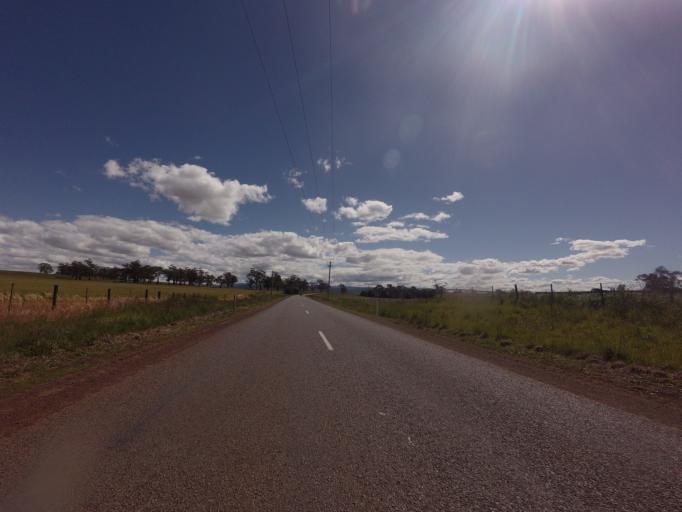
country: AU
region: Tasmania
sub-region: Northern Midlands
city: Evandale
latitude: -41.9420
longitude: 147.5378
